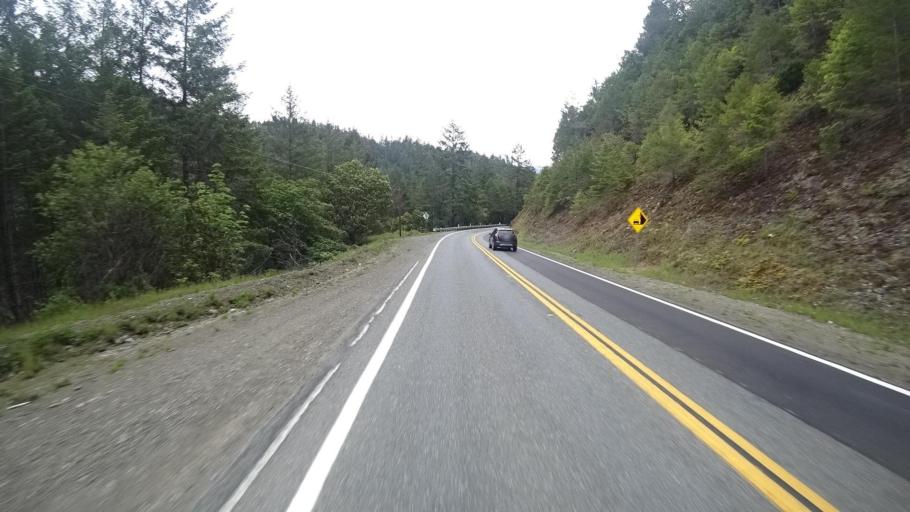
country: US
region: California
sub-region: Humboldt County
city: Willow Creek
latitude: 41.0009
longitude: -123.6315
